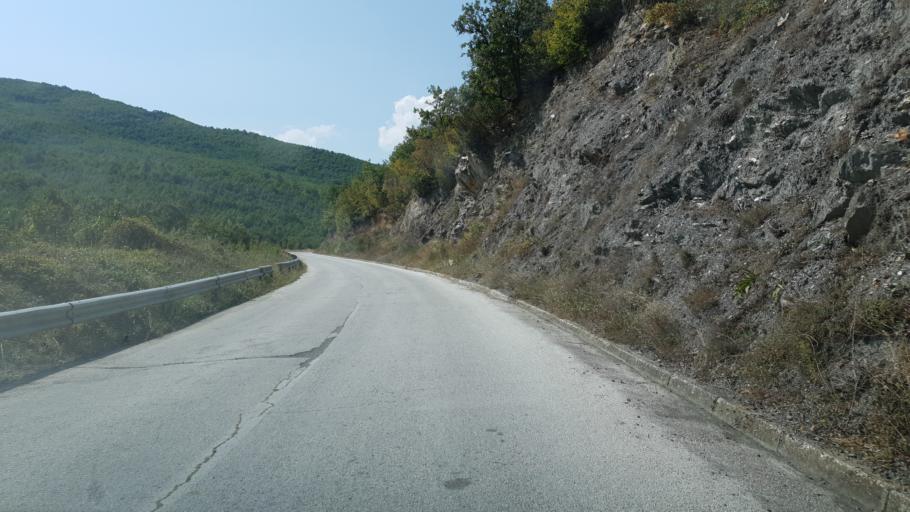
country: MK
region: Makedonski Brod
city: Samokov
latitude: 41.6665
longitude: 21.2314
